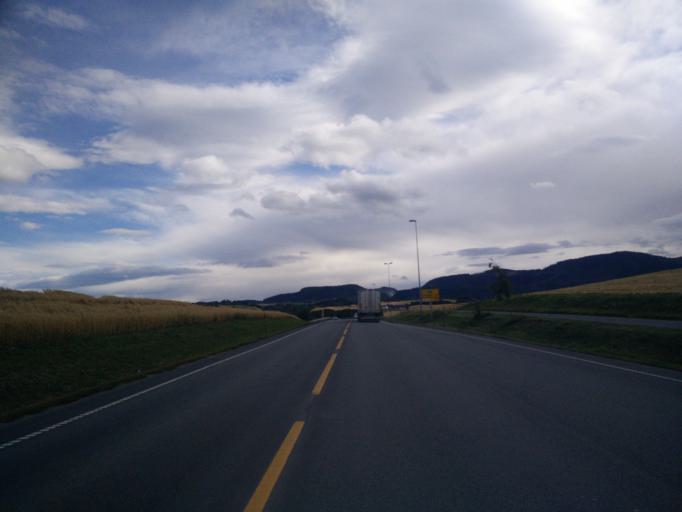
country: NO
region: Sor-Trondelag
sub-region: Melhus
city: Melhus
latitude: 63.3220
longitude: 10.3082
